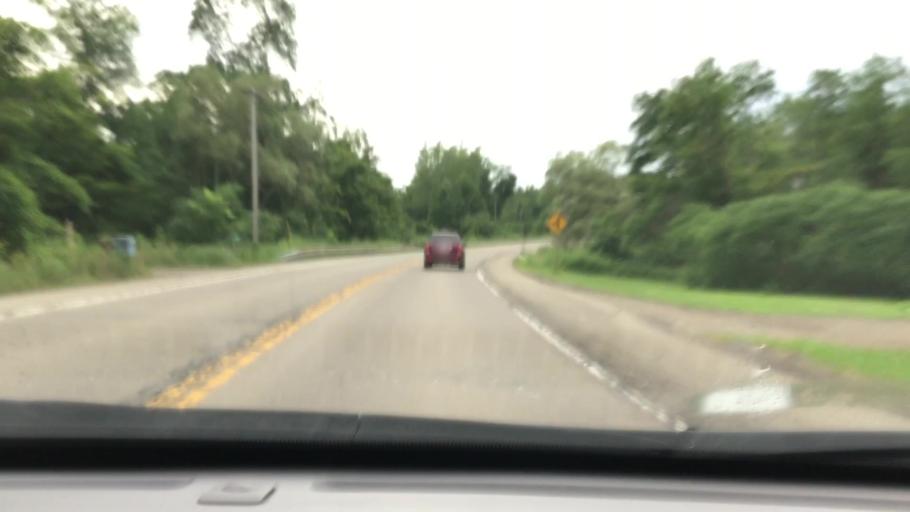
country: US
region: New York
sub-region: Erie County
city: Springville
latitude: 42.4173
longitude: -78.6932
